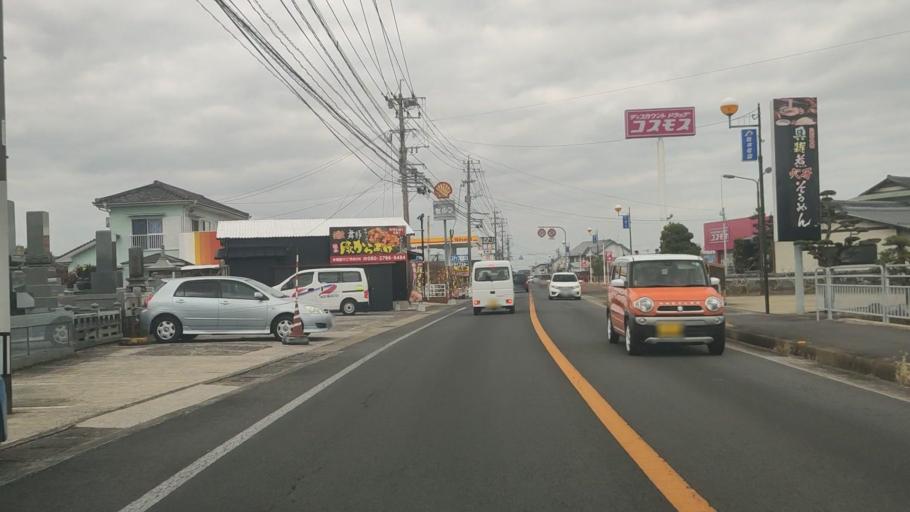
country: JP
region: Nagasaki
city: Shimabara
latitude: 32.8601
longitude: 130.3269
